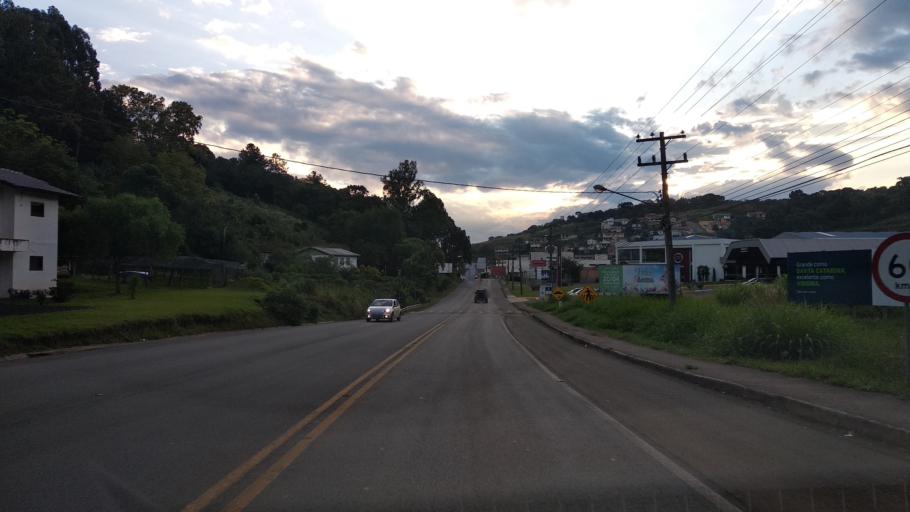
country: BR
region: Santa Catarina
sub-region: Videira
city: Videira
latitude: -27.0029
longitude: -51.1314
